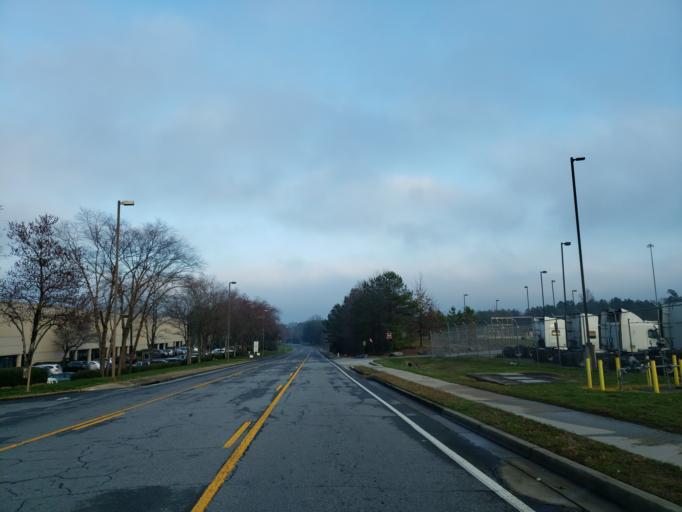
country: US
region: Georgia
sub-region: Cobb County
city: Kennesaw
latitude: 34.0106
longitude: -84.6011
